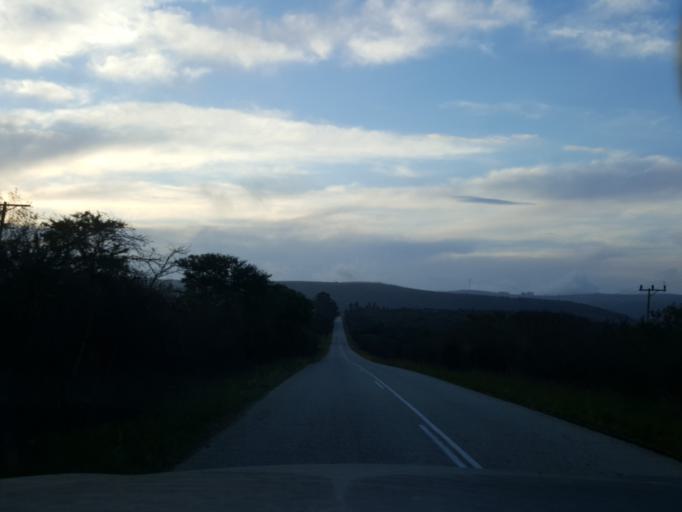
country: ZA
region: Eastern Cape
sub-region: Cacadu District Municipality
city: Grahamstown
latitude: -33.3894
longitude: 26.4740
